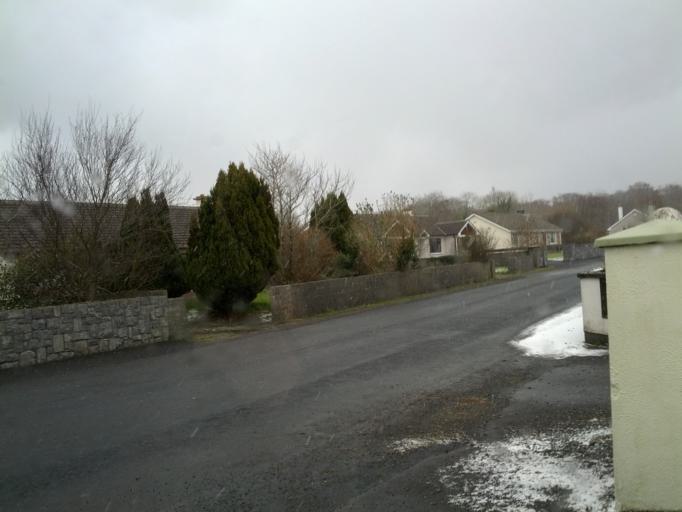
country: IE
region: Connaught
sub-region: County Galway
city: Oranmore
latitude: 53.2236
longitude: -8.8804
